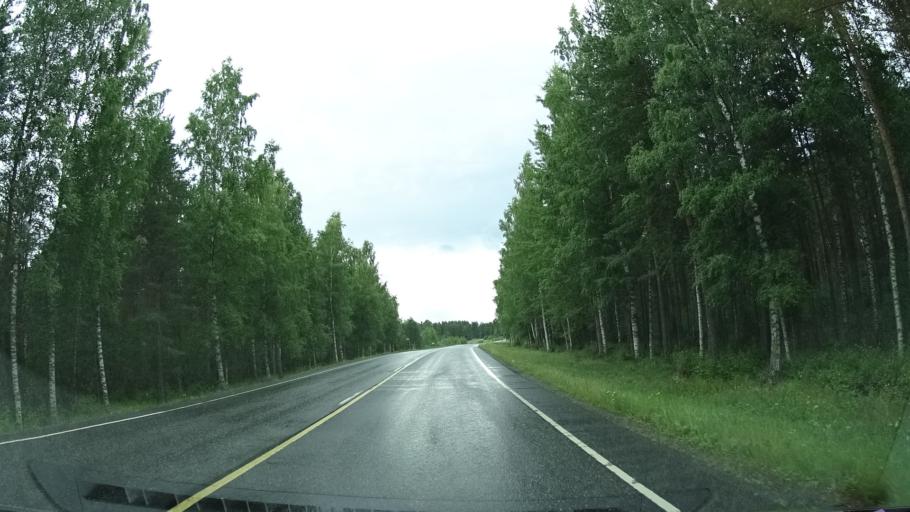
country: FI
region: Pirkanmaa
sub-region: Etelae-Pirkanmaa
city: Valkeakoski
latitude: 61.1633
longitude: 24.0407
